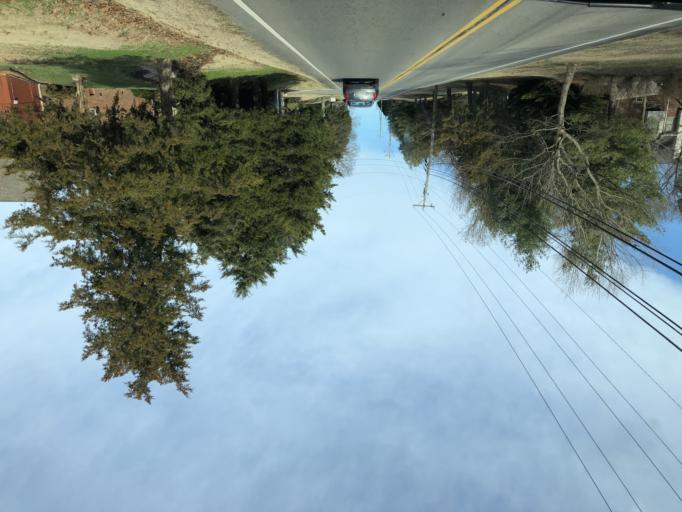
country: US
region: Tennessee
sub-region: Wilson County
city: Green Hill
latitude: 36.1566
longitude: -86.5862
